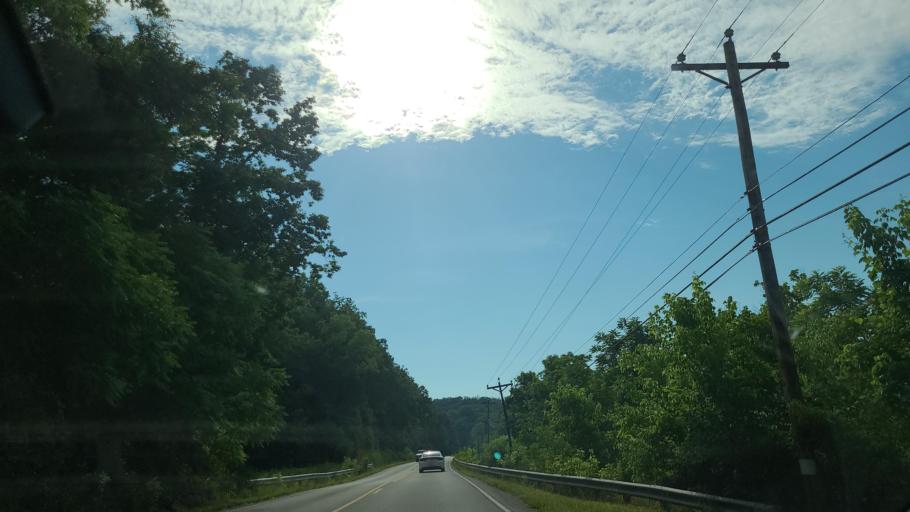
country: US
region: Kentucky
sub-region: Whitley County
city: Williamsburg
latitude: 36.7423
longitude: -84.0731
